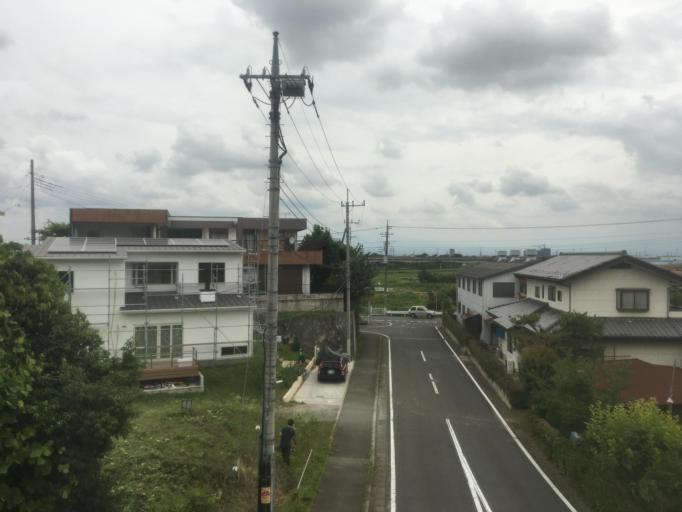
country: JP
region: Gunma
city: Fujioka
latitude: 36.2815
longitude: 139.0353
